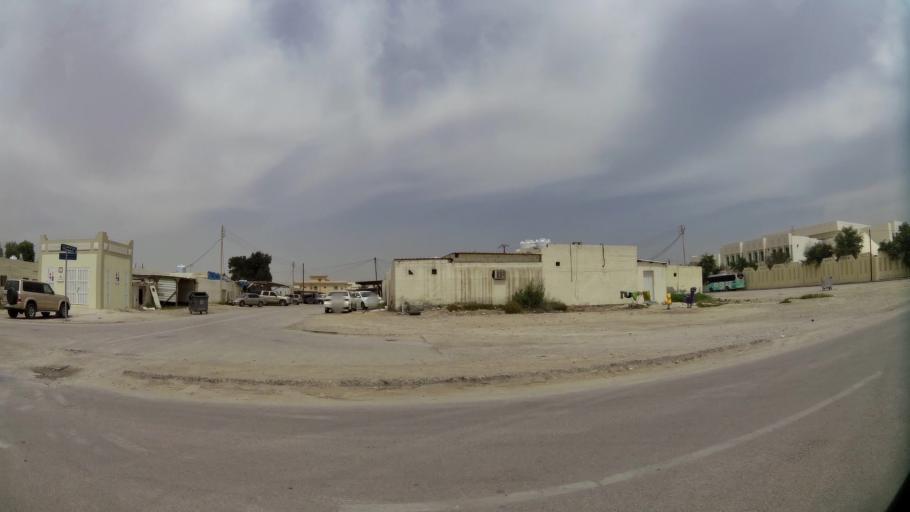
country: QA
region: Baladiyat ar Rayyan
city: Ar Rayyan
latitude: 25.2788
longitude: 51.4584
